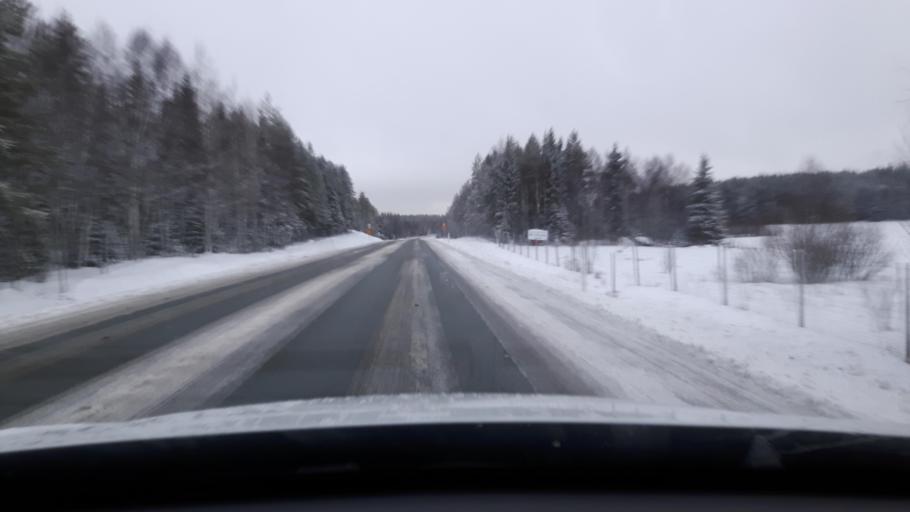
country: SE
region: Vaesterbotten
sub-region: Robertsfors Kommun
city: Robertsfors
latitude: 64.0287
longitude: 20.8416
